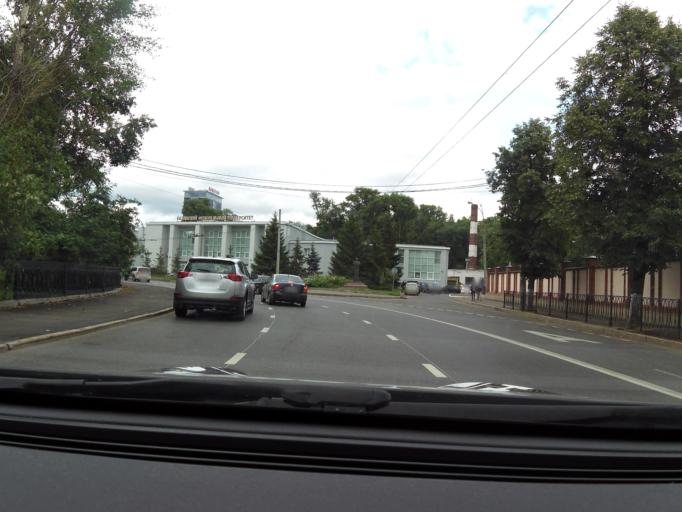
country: RU
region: Tatarstan
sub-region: Gorod Kazan'
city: Kazan
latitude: 55.7932
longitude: 49.1413
